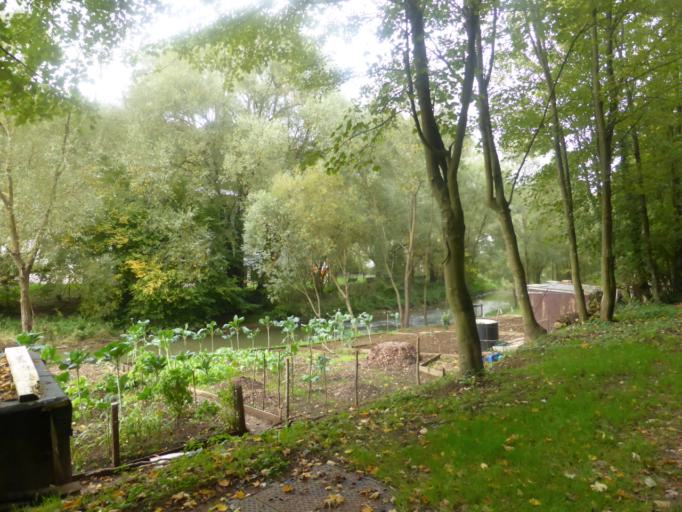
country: LU
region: Luxembourg
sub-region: Canton de Luxembourg
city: Hesperange
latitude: 49.5758
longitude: 6.1544
